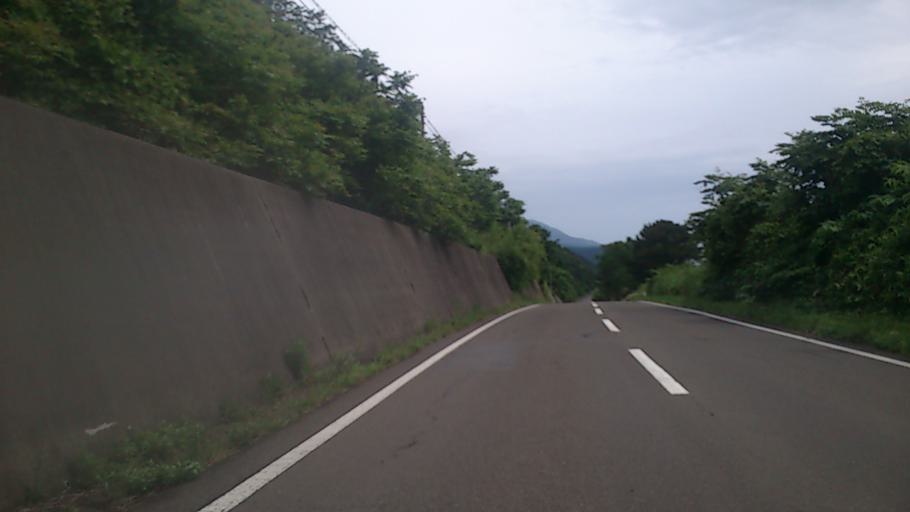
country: JP
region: Akita
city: Noshiromachi
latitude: 40.5199
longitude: 139.9513
